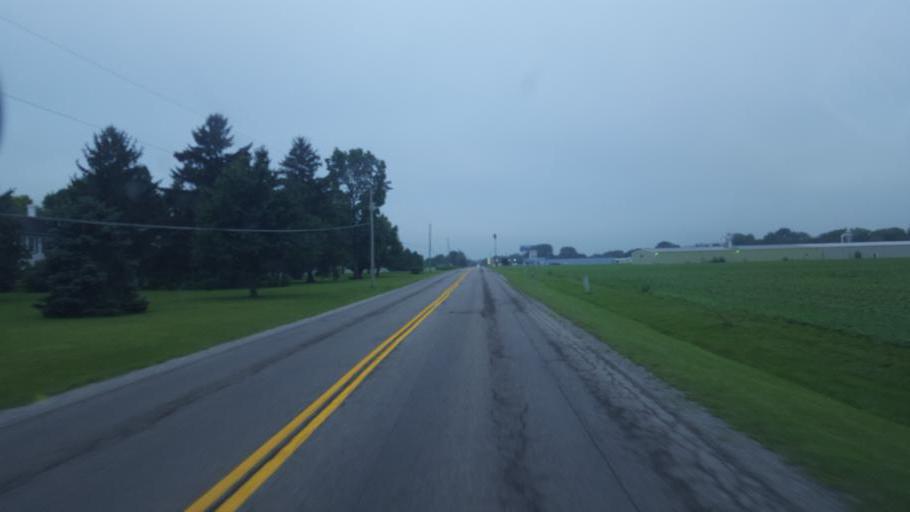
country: US
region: Ohio
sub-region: Fayette County
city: Washington Court House
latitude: 39.5414
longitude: -83.4042
